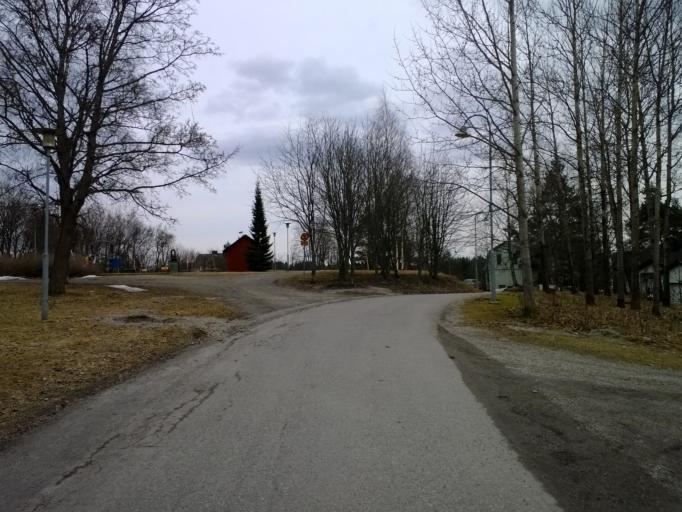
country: FI
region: Paijanne Tavastia
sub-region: Lahti
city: Lahti
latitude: 60.9737
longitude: 25.6614
